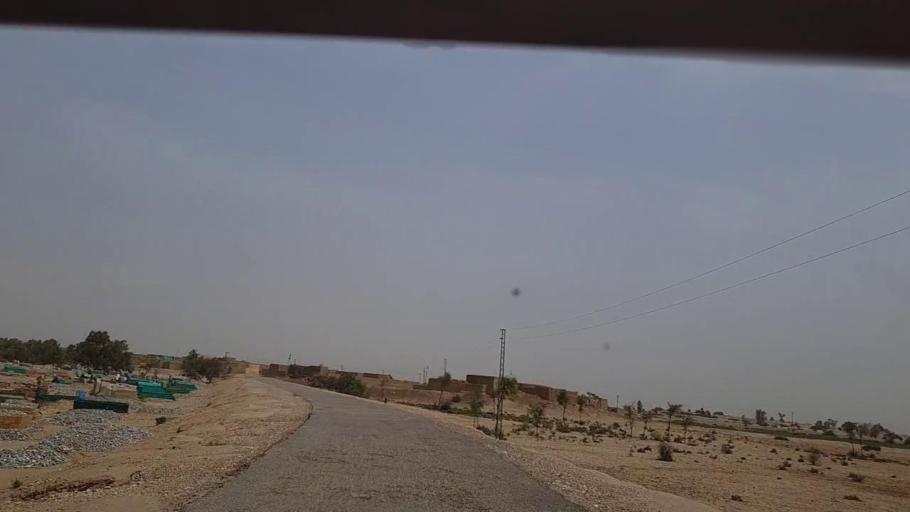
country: PK
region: Sindh
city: Phulji
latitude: 26.9990
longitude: 67.5035
